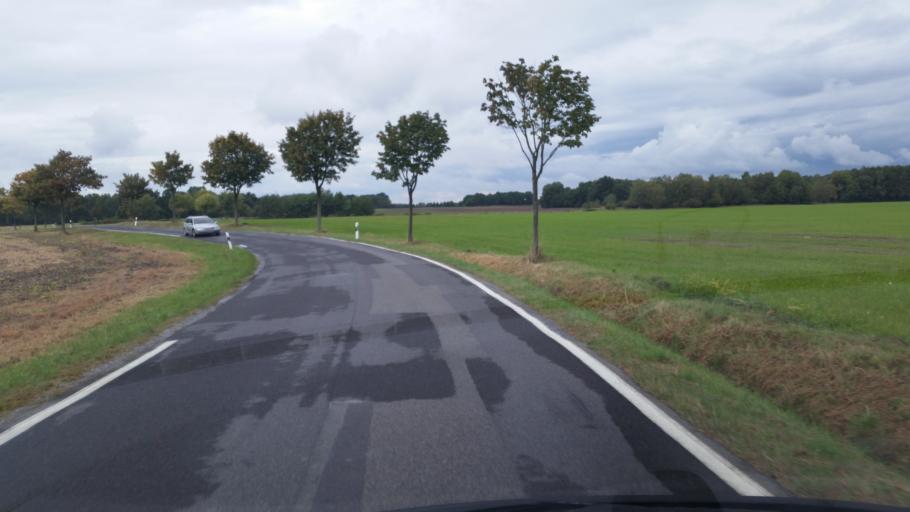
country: DE
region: Saxony
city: Neukirch
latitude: 51.3195
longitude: 14.0250
